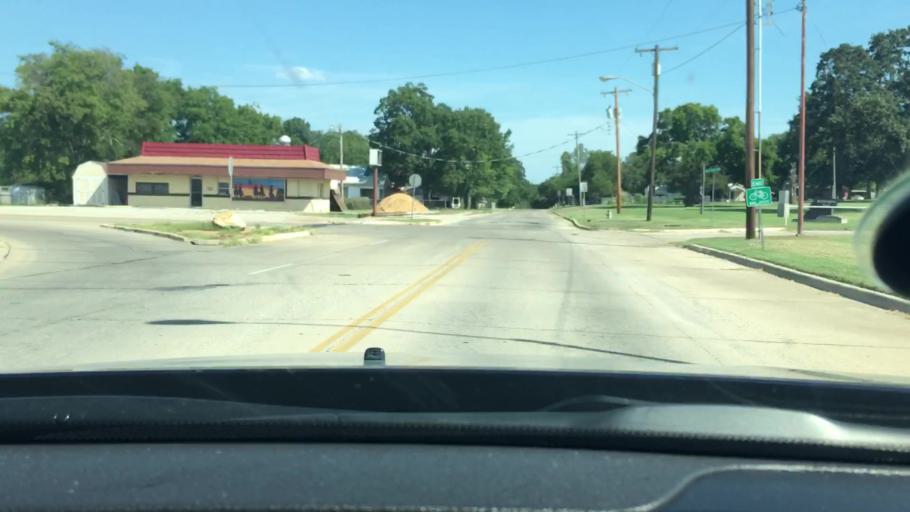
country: US
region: Oklahoma
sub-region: Carter County
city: Ardmore
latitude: 34.1626
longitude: -97.1215
